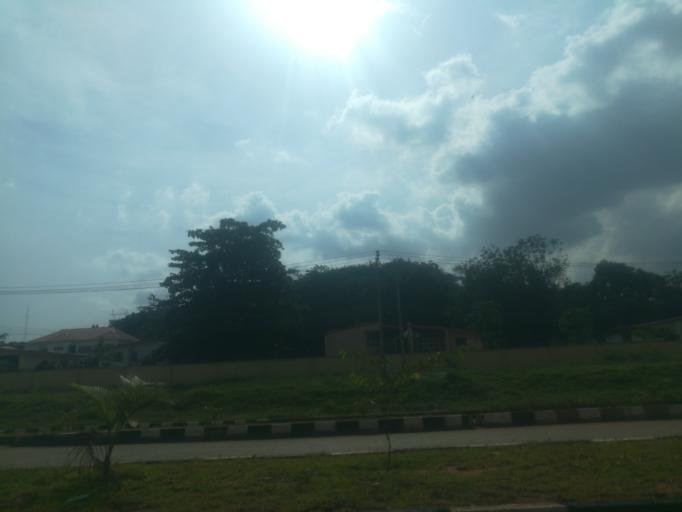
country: NG
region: Ogun
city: Abeokuta
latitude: 7.1289
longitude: 3.3554
